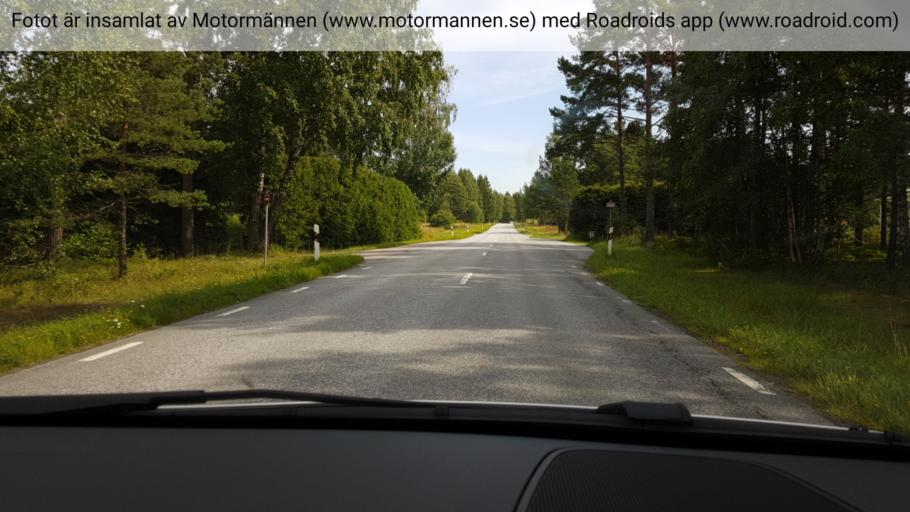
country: SE
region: Uppsala
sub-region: Osthammars Kommun
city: OEsthammar
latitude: 60.2396
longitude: 18.3576
